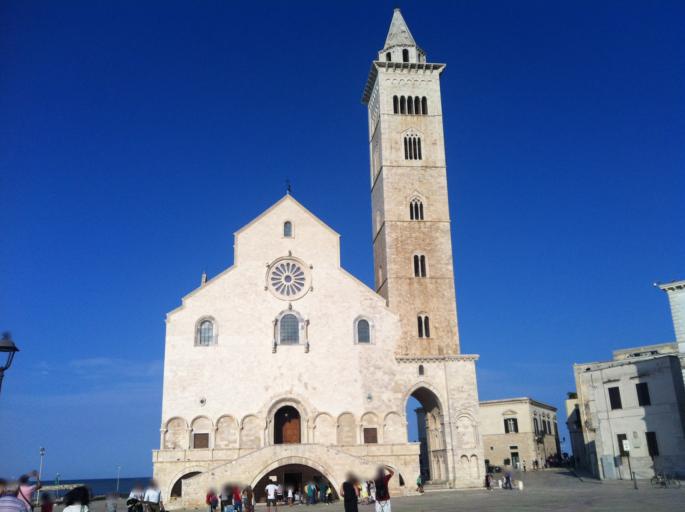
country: IT
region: Apulia
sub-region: Provincia di Barletta - Andria - Trani
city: Trani
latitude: 41.2819
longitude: 16.4175
